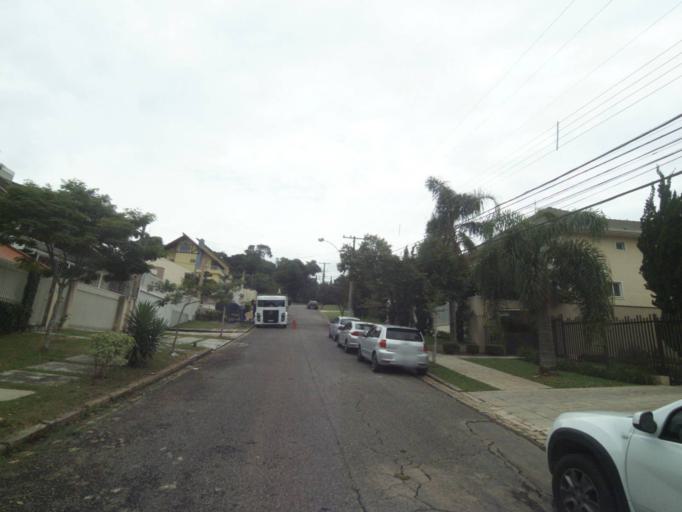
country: BR
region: Parana
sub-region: Curitiba
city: Curitiba
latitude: -25.4042
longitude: -49.2845
